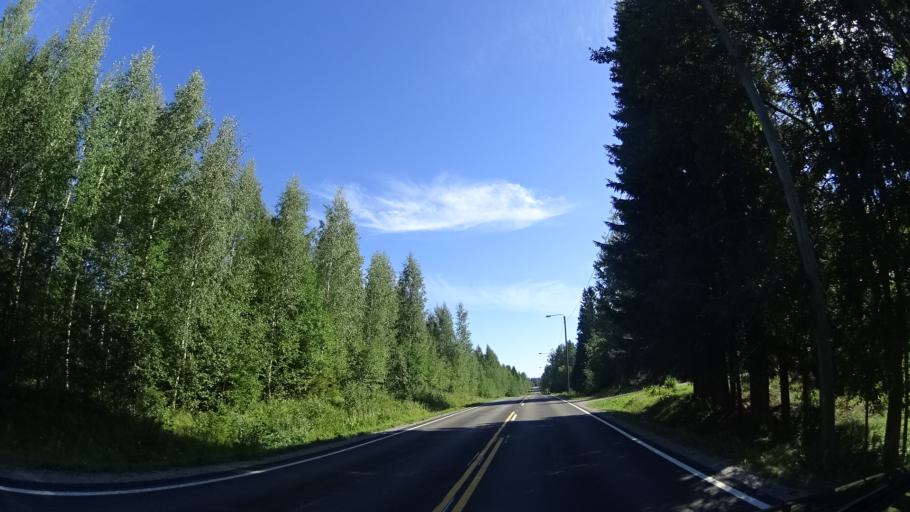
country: FI
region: Central Finland
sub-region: Jyvaeskylae
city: Uurainen
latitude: 62.4826
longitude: 25.4254
